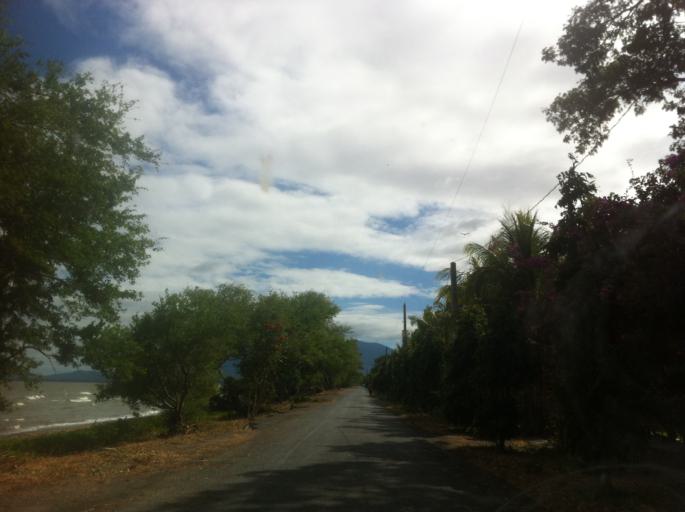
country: NI
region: Granada
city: Granada
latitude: 11.9814
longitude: -85.9408
